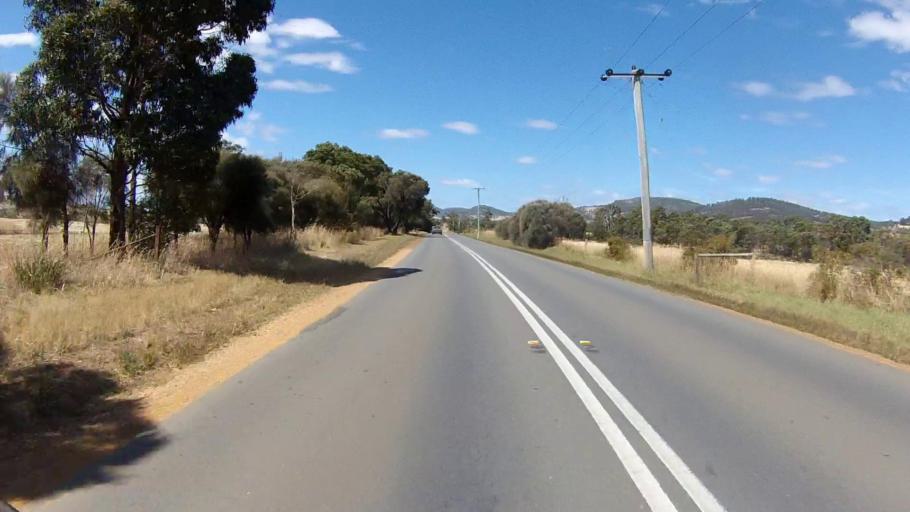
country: AU
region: Tasmania
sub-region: Clarence
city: Cambridge
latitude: -42.7644
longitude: 147.4149
